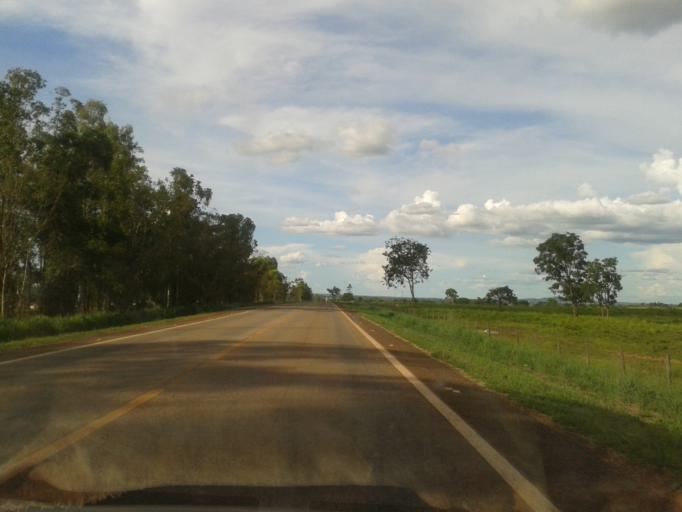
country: BR
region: Goias
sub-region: Crixas
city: Crixas
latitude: -14.2500
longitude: -50.3968
